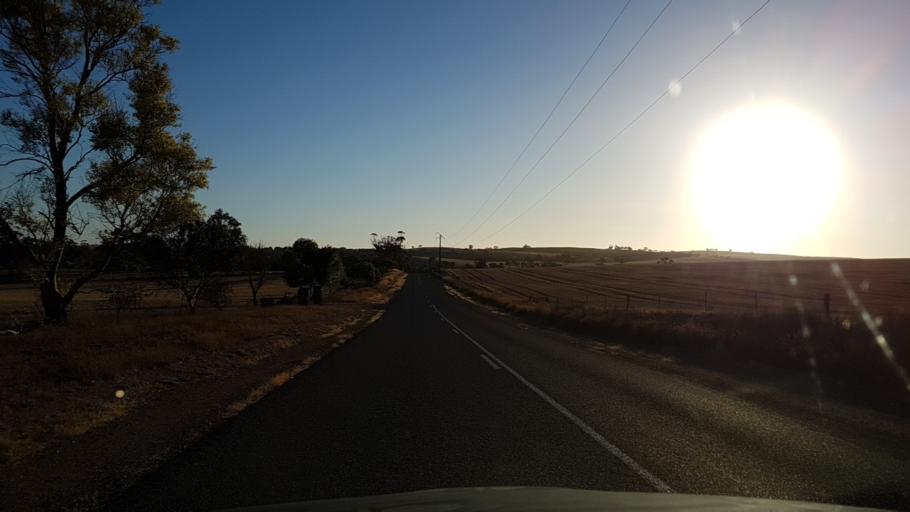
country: AU
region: South Australia
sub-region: Clare and Gilbert Valleys
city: Clare
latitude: -34.0214
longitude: 138.6965
